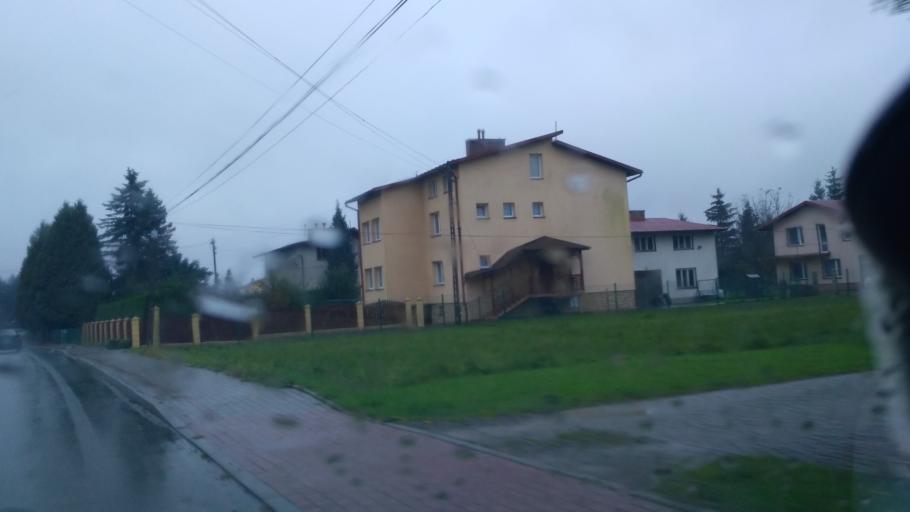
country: PL
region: Subcarpathian Voivodeship
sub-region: Powiat krosnienski
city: Korczyna
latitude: 49.7080
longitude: 21.8119
